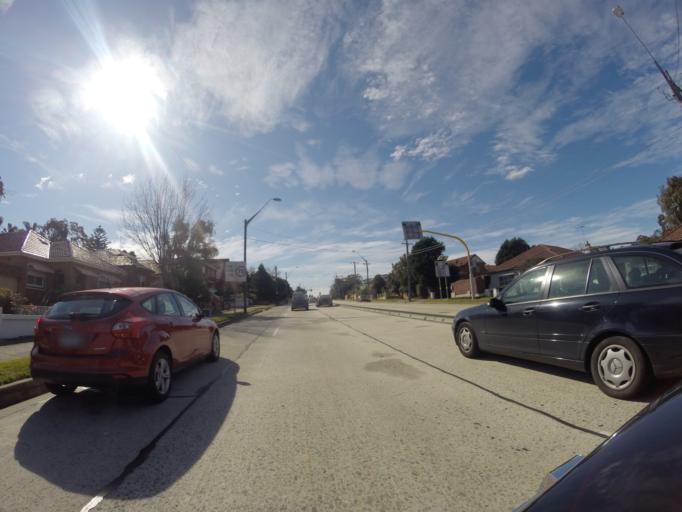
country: AU
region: New South Wales
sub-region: Kogarah
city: Kogarah
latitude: -33.9853
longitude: 151.1130
